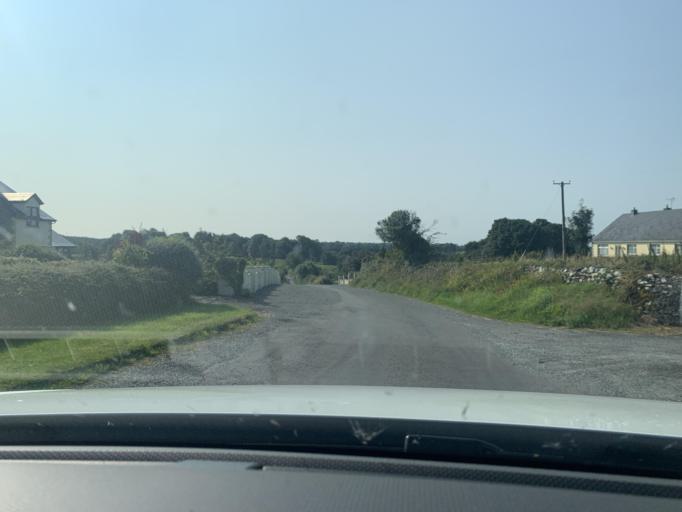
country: IE
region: Connaught
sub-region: Maigh Eo
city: Ballyhaunis
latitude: 53.7852
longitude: -8.7404
